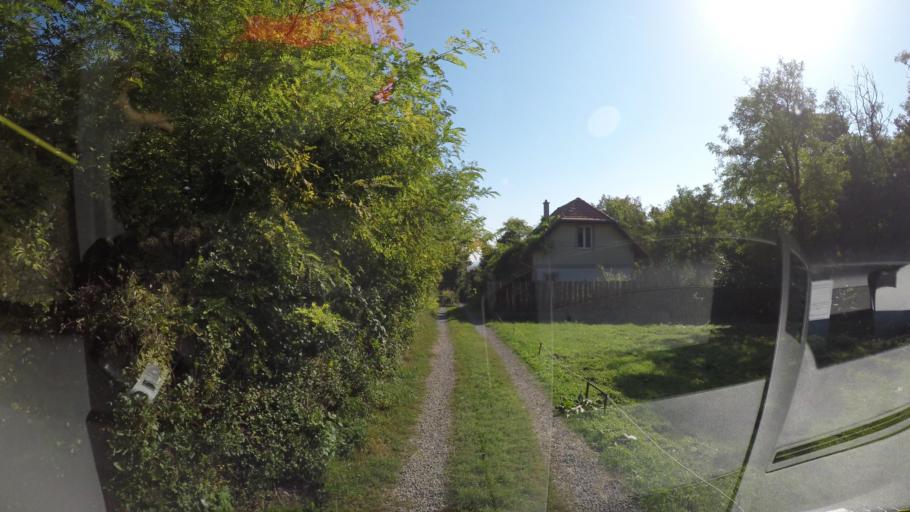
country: HU
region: Pest
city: Leanyfalu
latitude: 47.7272
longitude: 19.0831
